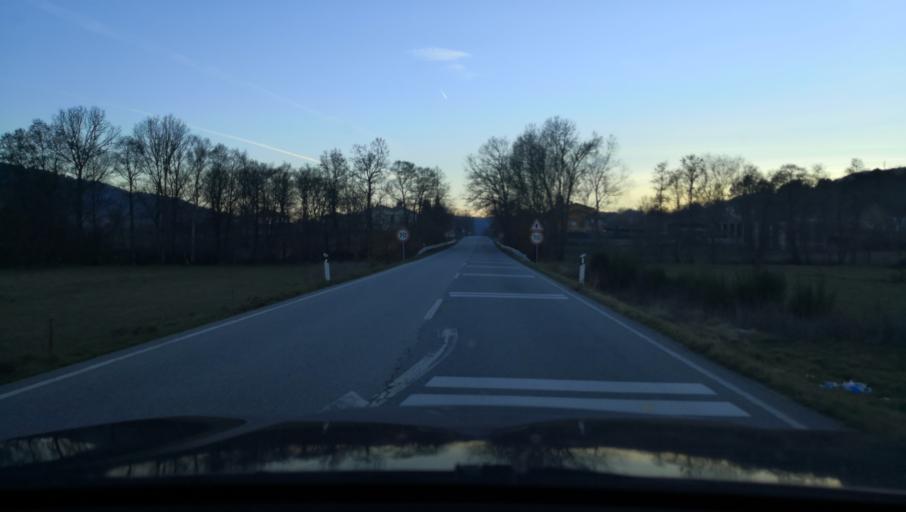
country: PT
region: Vila Real
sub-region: Vila Pouca de Aguiar
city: Vila Pouca de Aguiar
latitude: 41.4341
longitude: -7.6786
